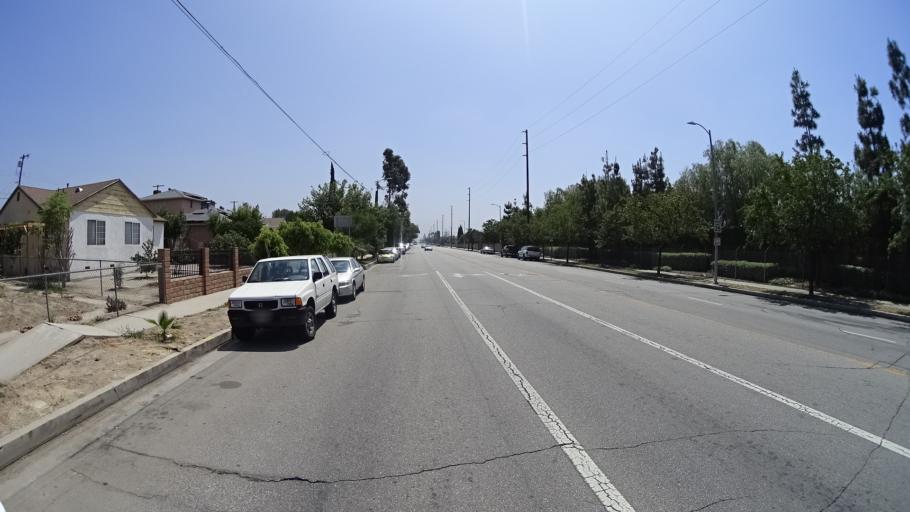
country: US
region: California
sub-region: Los Angeles County
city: North Hollywood
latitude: 34.2085
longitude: -118.4046
